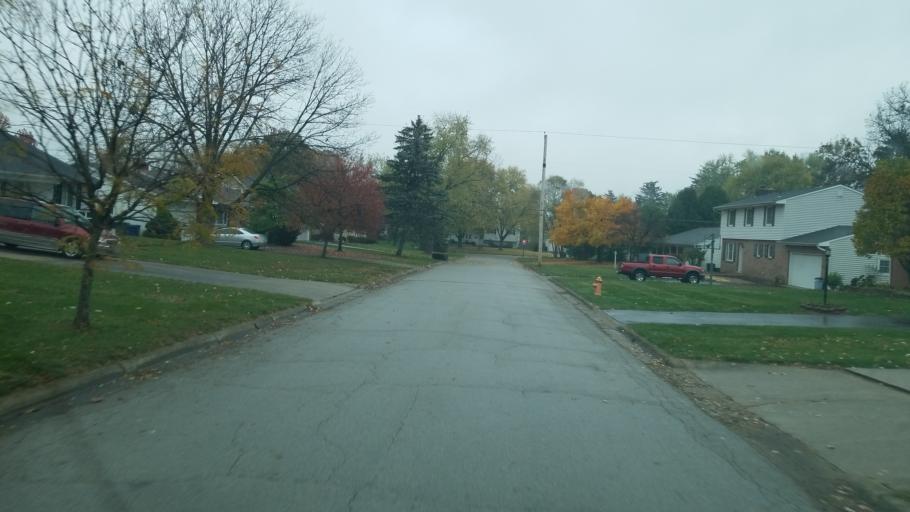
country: US
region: Ohio
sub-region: Franklin County
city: Upper Arlington
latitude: 40.0433
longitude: -83.0476
